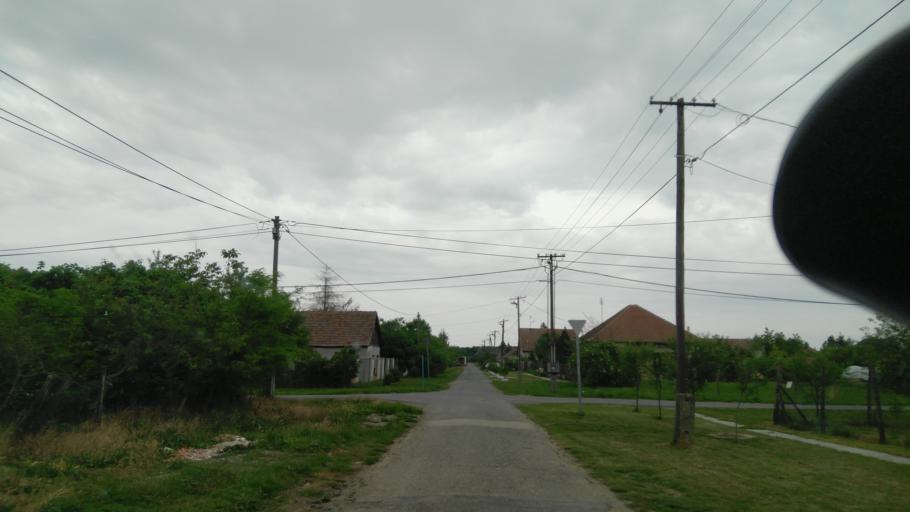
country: HU
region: Bekes
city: Doboz
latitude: 46.7268
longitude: 21.2477
